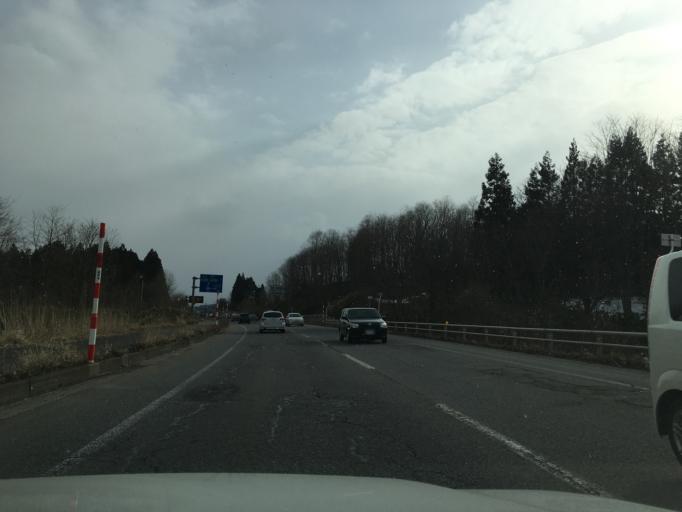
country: JP
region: Aomori
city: Namioka
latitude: 40.7639
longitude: 140.5877
